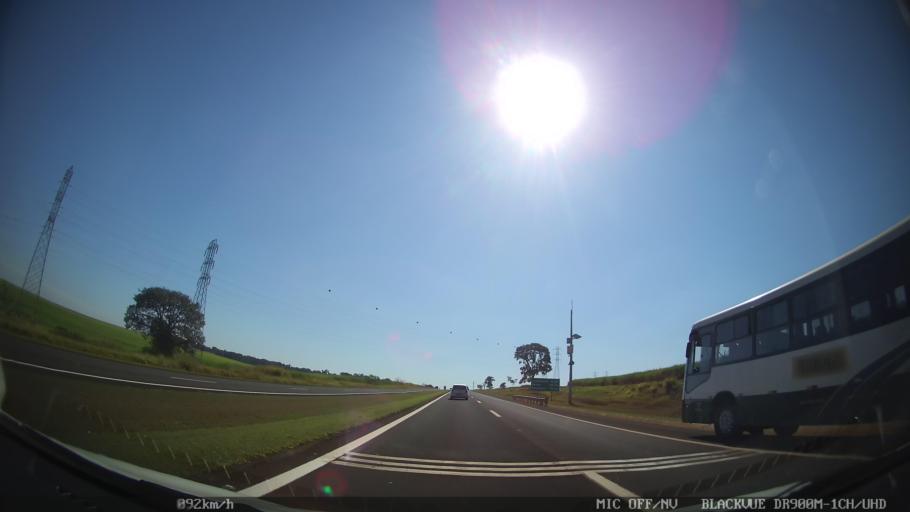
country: BR
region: Sao Paulo
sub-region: Ribeirao Preto
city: Ribeirao Preto
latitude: -21.1893
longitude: -47.8867
